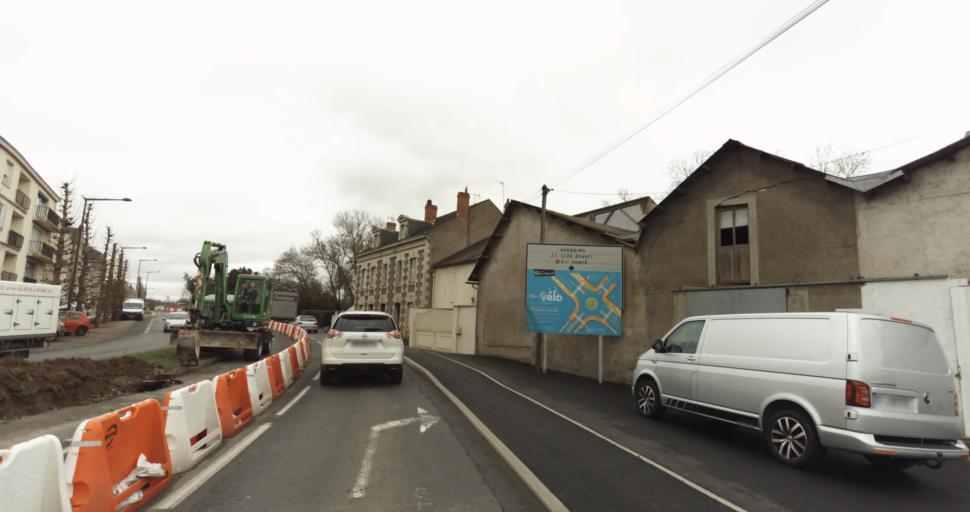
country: FR
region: Pays de la Loire
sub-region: Departement de Maine-et-Loire
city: Saumur
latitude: 47.2543
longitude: -0.0866
